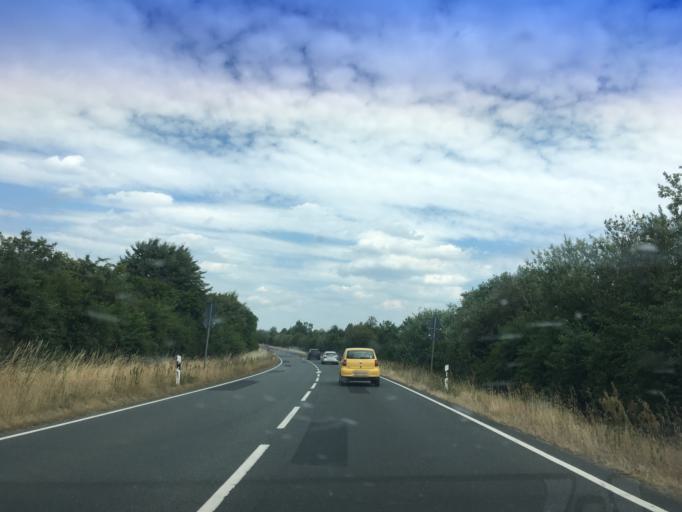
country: DE
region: Saxony
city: Goerlitz
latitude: 51.1564
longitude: 14.9515
